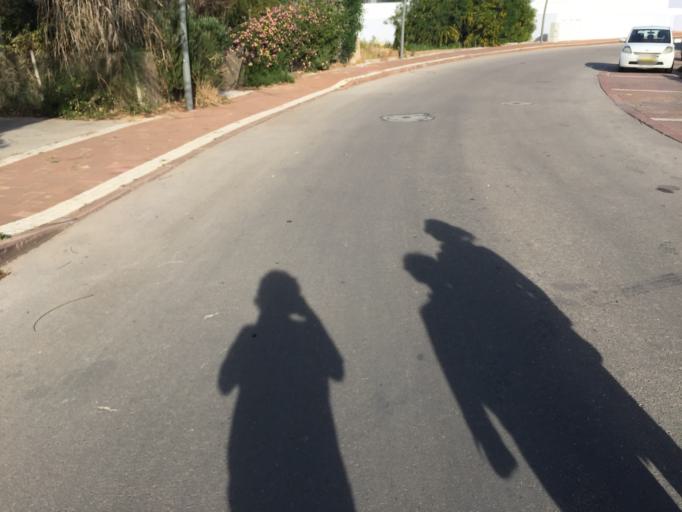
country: IL
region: Haifa
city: Qesarya
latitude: 32.5146
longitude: 34.9021
